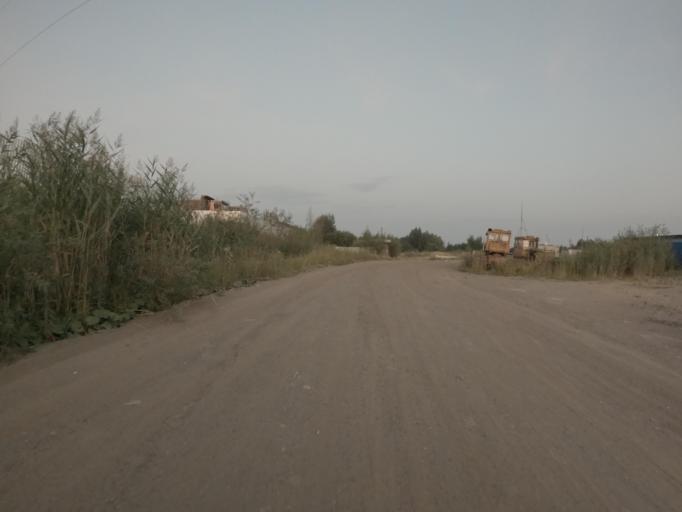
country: RU
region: Leningrad
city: Yanino Vtoroye
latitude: 59.9346
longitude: 30.5956
